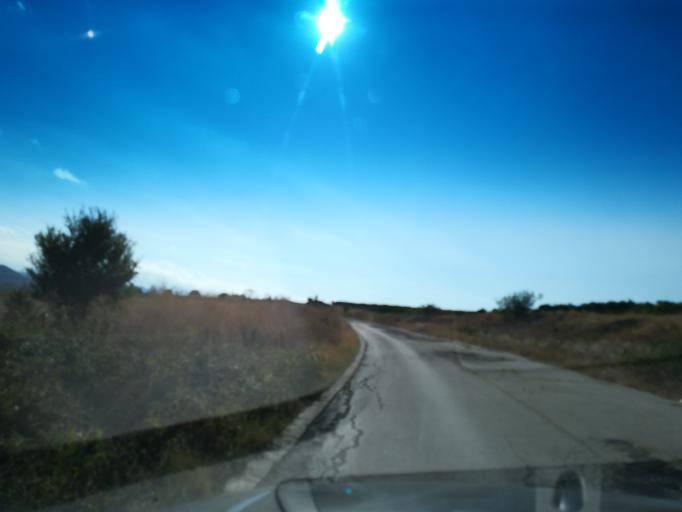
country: BG
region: Khaskovo
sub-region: Obshtina Mineralni Bani
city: Mineralni Bani
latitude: 41.9724
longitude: 25.3482
